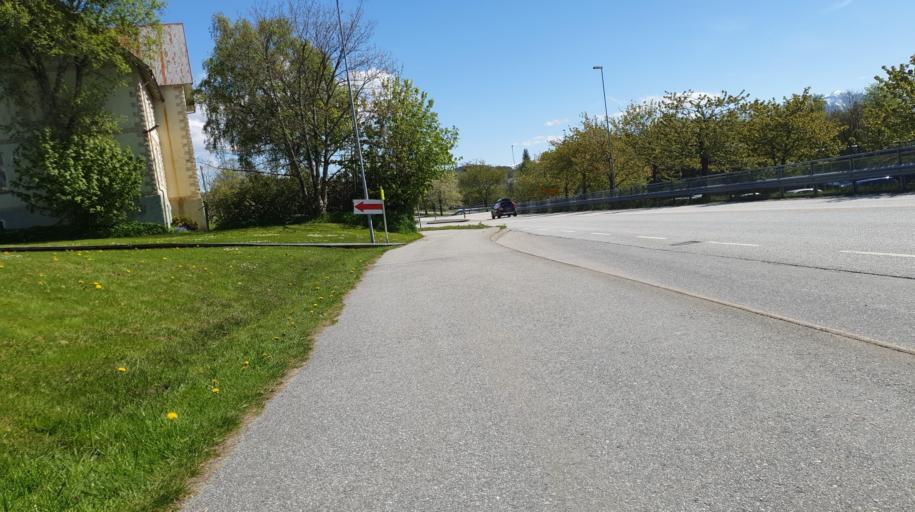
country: NO
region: More og Romsdal
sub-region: Sula
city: Langevag
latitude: 62.4714
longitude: 6.2357
